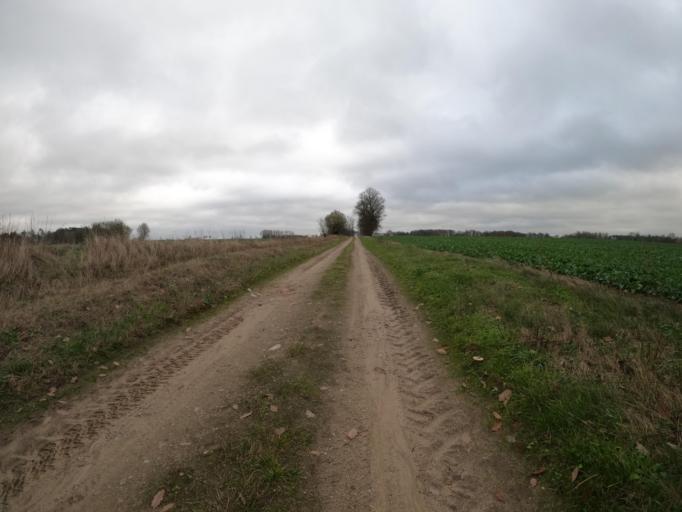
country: PL
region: West Pomeranian Voivodeship
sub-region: Powiat walecki
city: Tuczno
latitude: 53.2744
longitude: 16.1695
